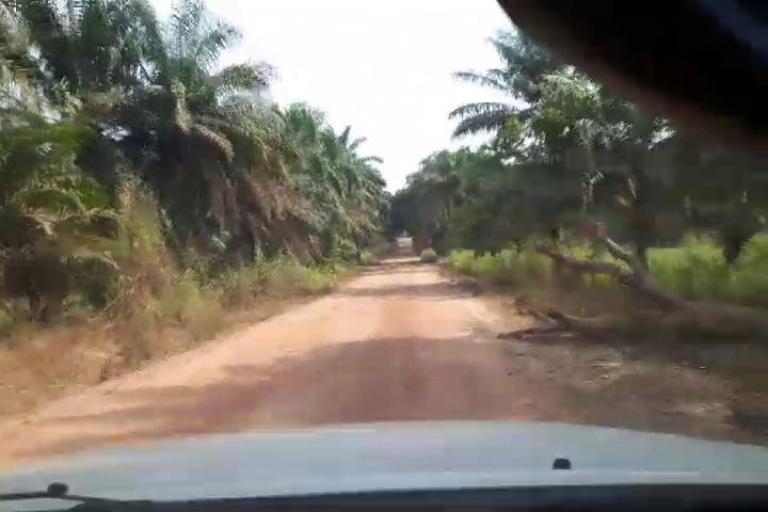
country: SL
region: Northern Province
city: Masingbi
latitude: 8.7884
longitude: -11.8707
